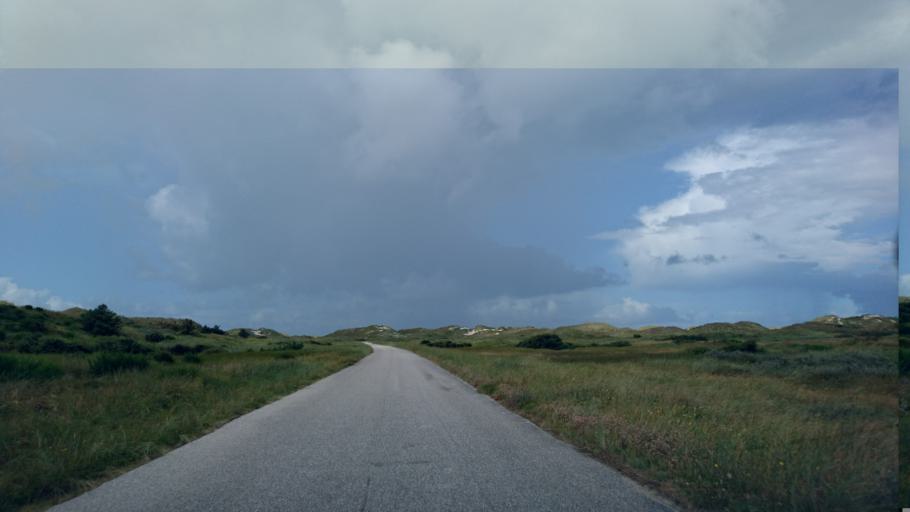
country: DK
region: North Denmark
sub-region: Frederikshavn Kommune
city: Skagen
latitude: 57.7198
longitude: 10.5156
